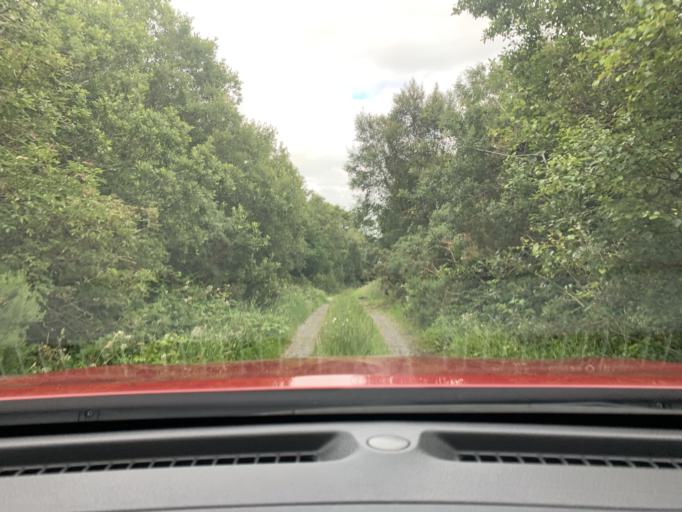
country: IE
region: Connaught
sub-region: County Leitrim
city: Kinlough
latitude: 54.4558
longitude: -8.3590
